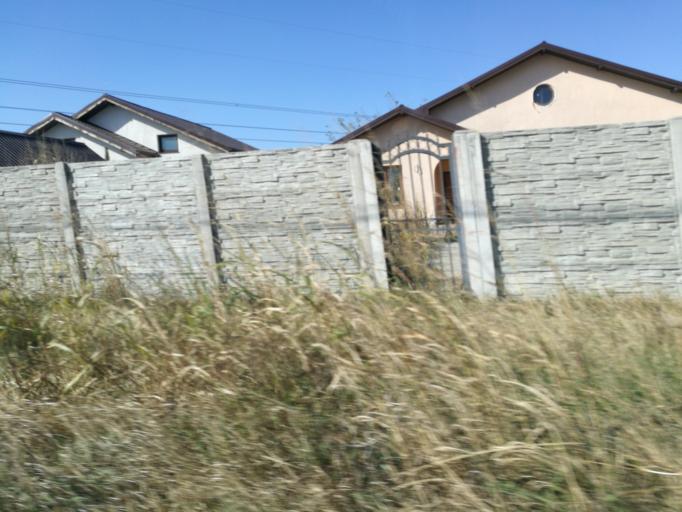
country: RO
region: Giurgiu
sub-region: Comuna Joita
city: Bacu
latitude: 44.4733
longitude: 25.8880
